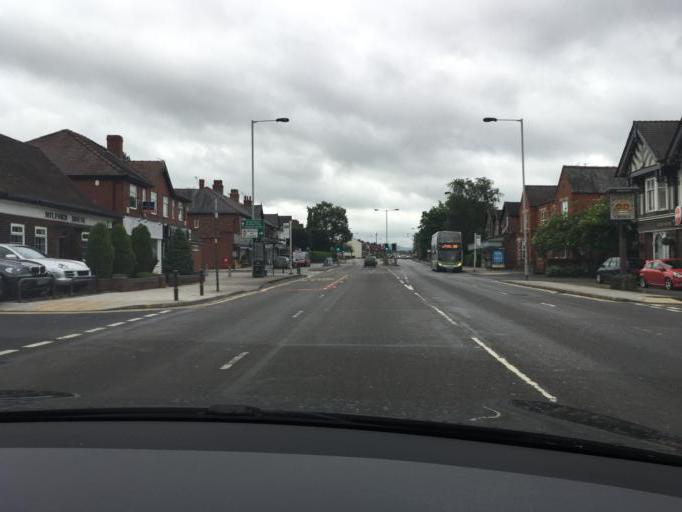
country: GB
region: England
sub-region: Borough of Stockport
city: Hazel Grove
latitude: 53.3873
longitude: -2.1331
